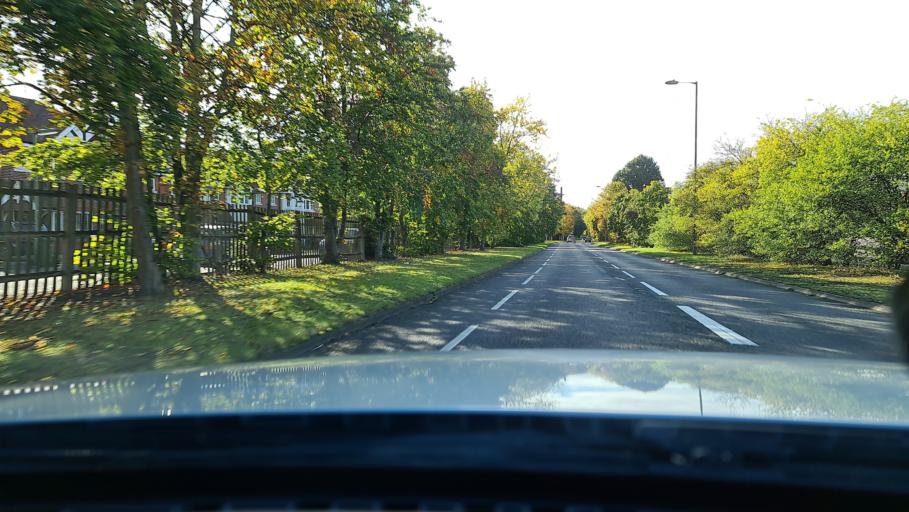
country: GB
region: England
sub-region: Surrey
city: Walton-on-Thames
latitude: 51.3686
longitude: -0.4047
